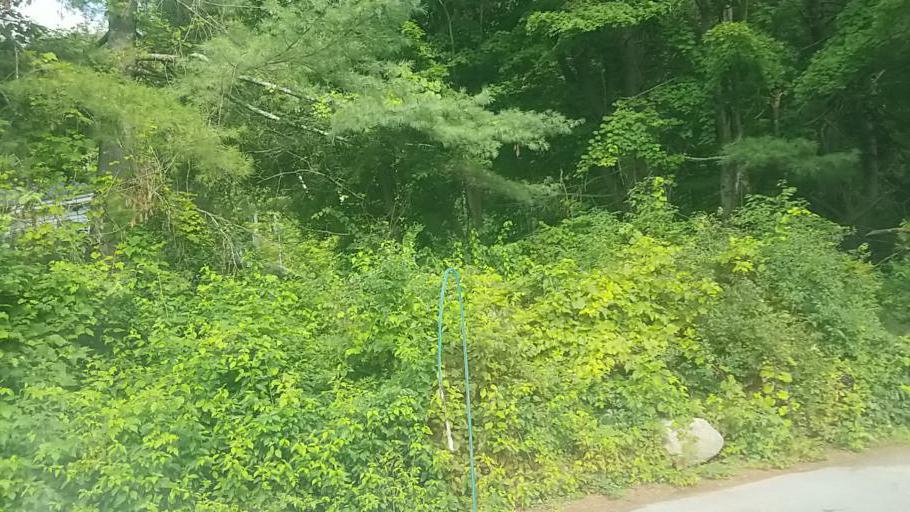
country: US
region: New York
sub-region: Fulton County
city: Broadalbin
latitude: 43.0804
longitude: -74.2234
